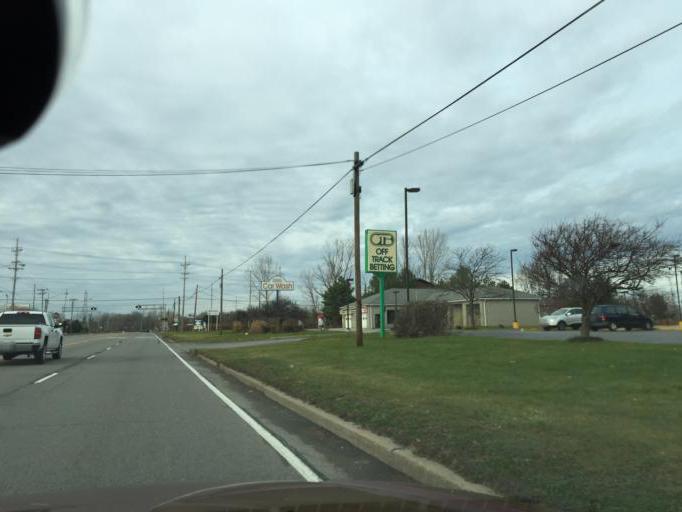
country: US
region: New York
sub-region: Monroe County
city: Rochester
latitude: 43.0909
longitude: -77.6466
